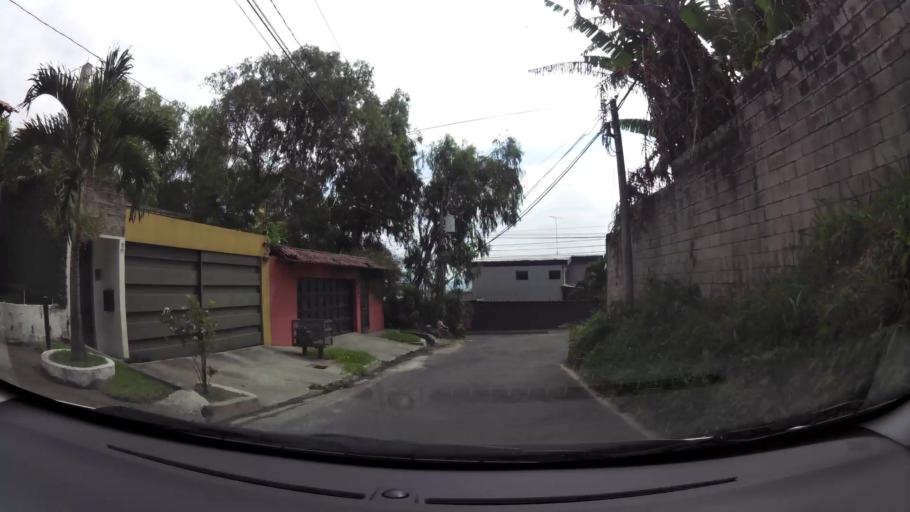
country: SV
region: La Libertad
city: Santa Tecla
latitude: 13.7080
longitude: -89.2616
